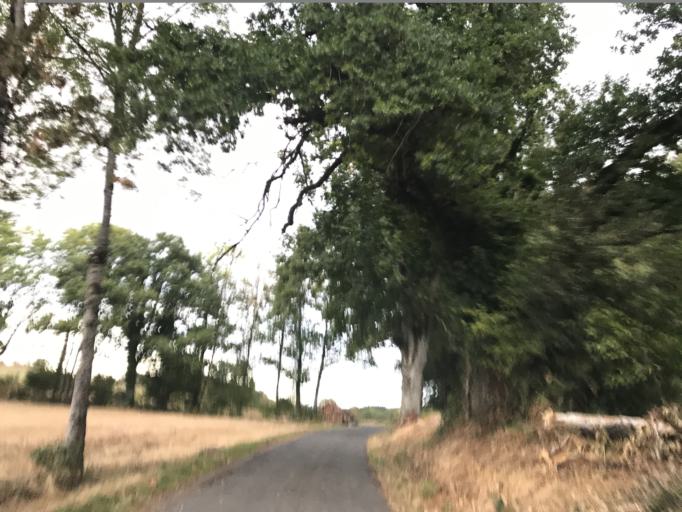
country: FR
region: Auvergne
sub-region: Departement du Puy-de-Dome
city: Thiers
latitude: 45.8398
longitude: 3.5848
